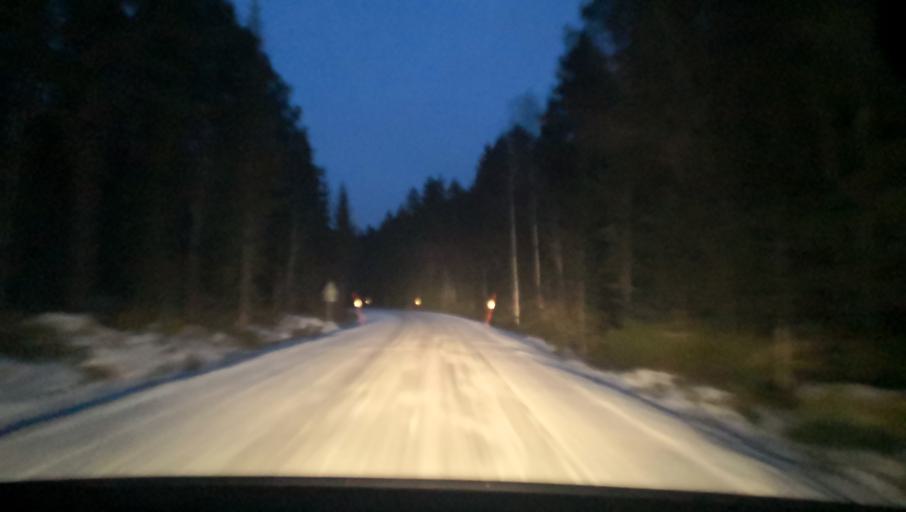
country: SE
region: Uppsala
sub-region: Heby Kommun
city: Tarnsjo
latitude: 60.2473
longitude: 16.7276
